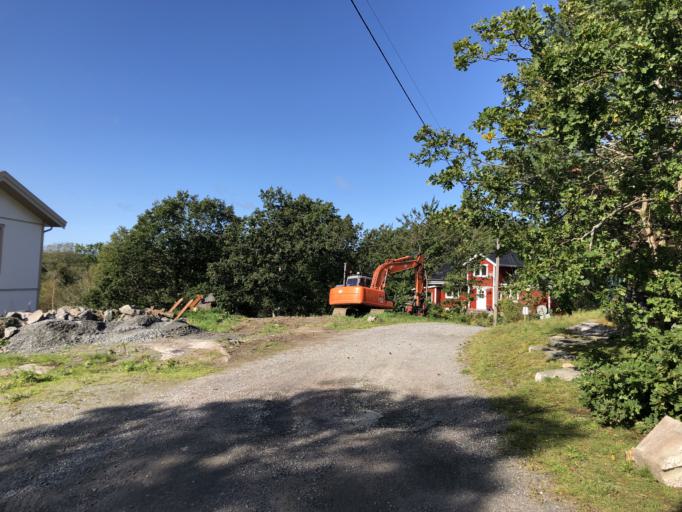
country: SE
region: Vaestra Goetaland
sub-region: Goteborg
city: Torslanda
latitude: 57.7440
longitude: 11.8159
